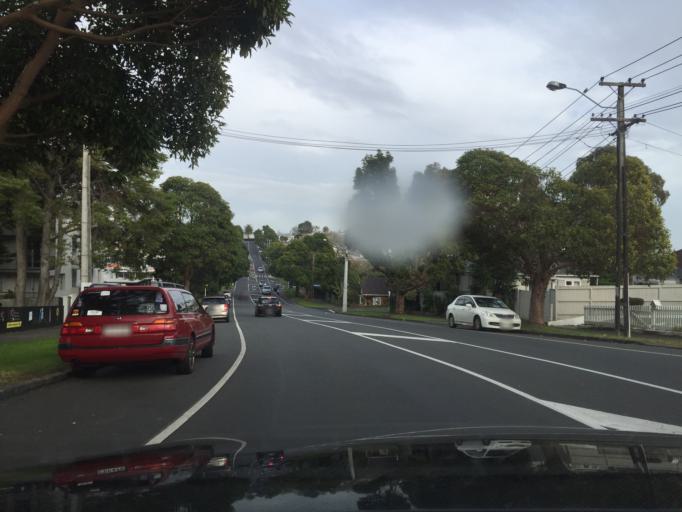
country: NZ
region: Auckland
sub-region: Auckland
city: Auckland
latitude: -36.8536
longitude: 174.7342
